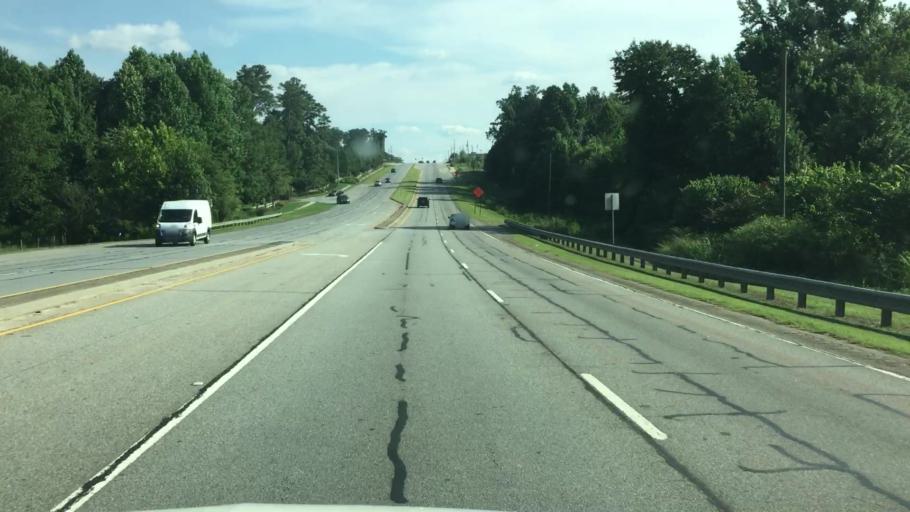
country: US
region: Georgia
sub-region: Gwinnett County
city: Lawrenceville
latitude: 33.9114
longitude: -84.0020
